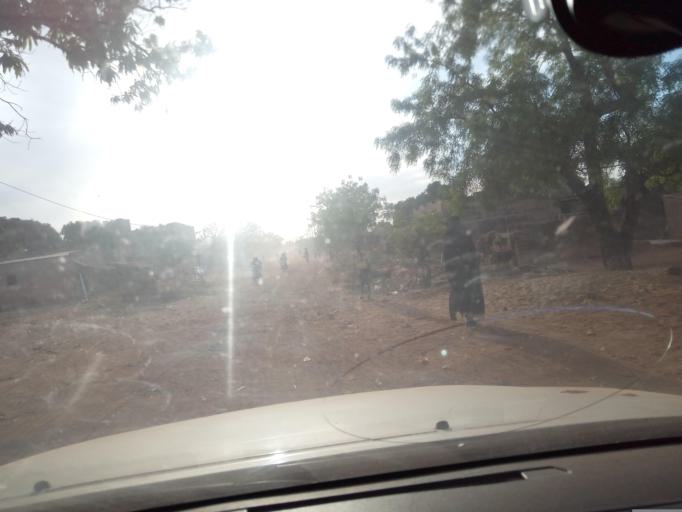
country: ML
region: Sikasso
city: Sikasso
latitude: 11.3136
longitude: -5.6490
